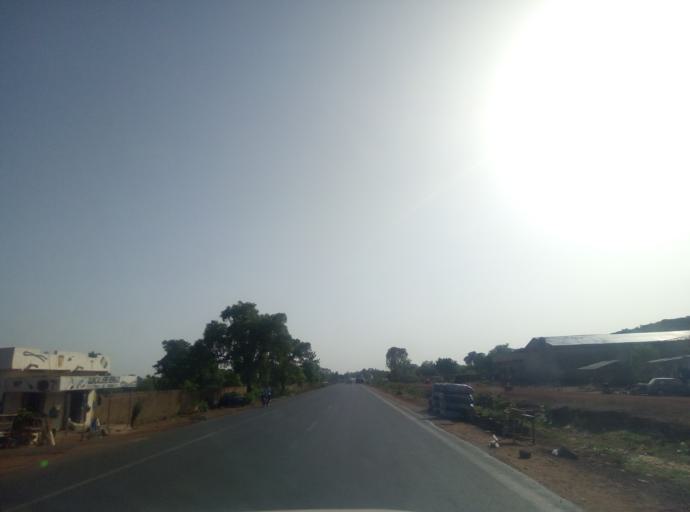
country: ML
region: Bamako
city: Bamako
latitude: 12.5811
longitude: -7.7764
